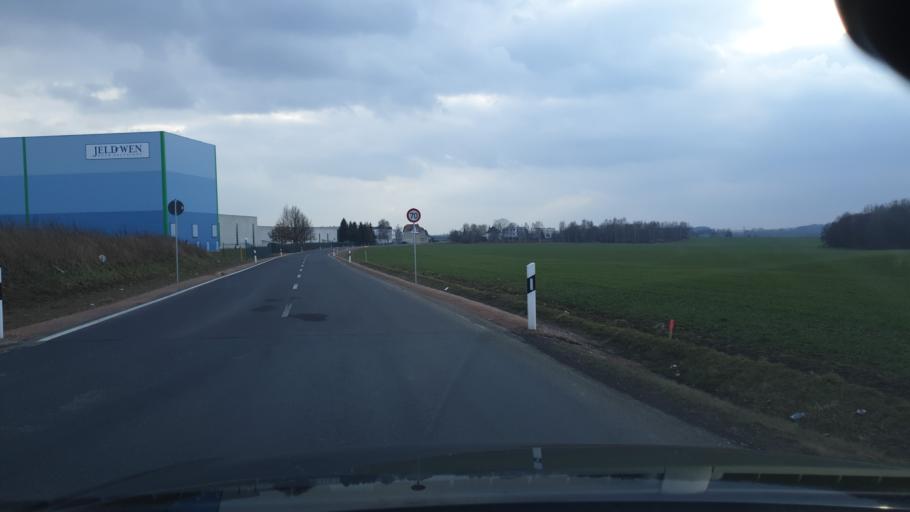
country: DE
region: Saxony
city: Altmittweida
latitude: 50.9917
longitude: 12.9502
